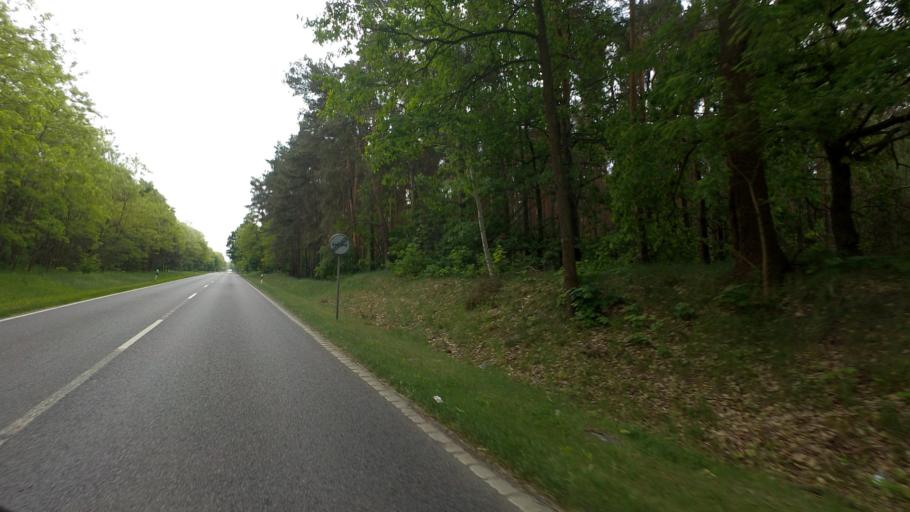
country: DE
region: Brandenburg
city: Lieberose
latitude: 51.9653
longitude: 14.3161
